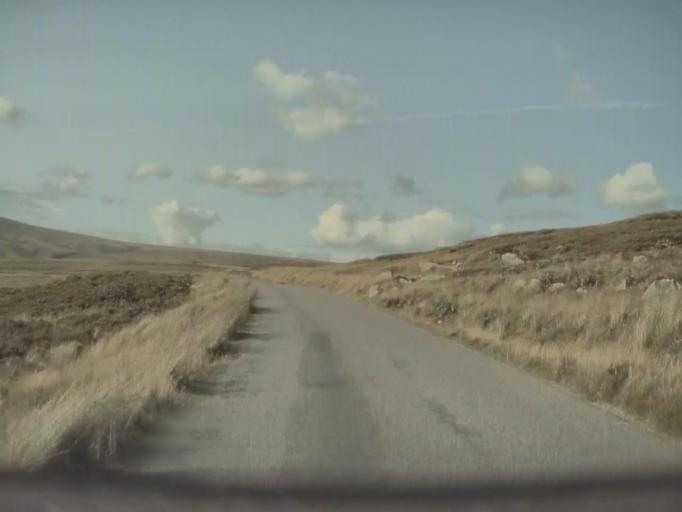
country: IE
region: Leinster
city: Ballyboden
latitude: 53.1503
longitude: -6.3123
